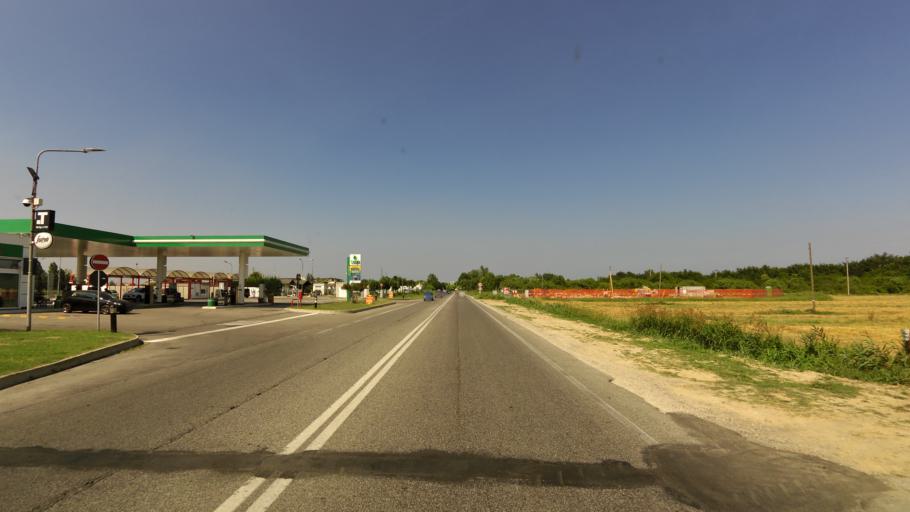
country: IT
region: Emilia-Romagna
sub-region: Provincia di Ravenna
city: Porto Fuori
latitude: 44.4070
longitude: 12.2266
